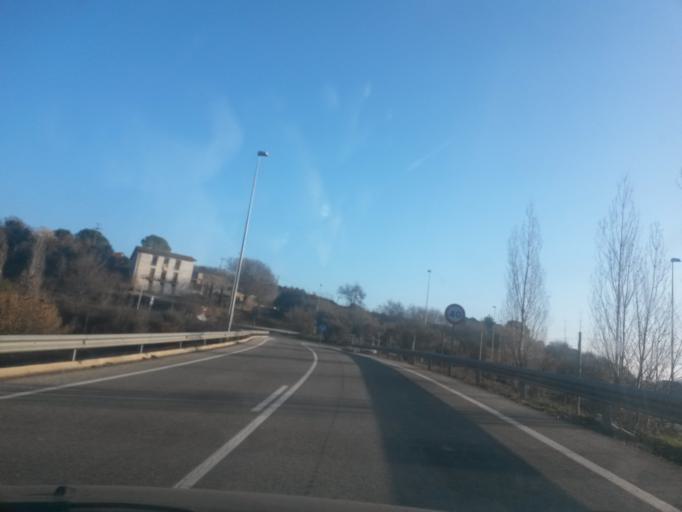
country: ES
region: Catalonia
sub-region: Provincia de Girona
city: Argelaguer
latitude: 42.2172
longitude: 2.6390
